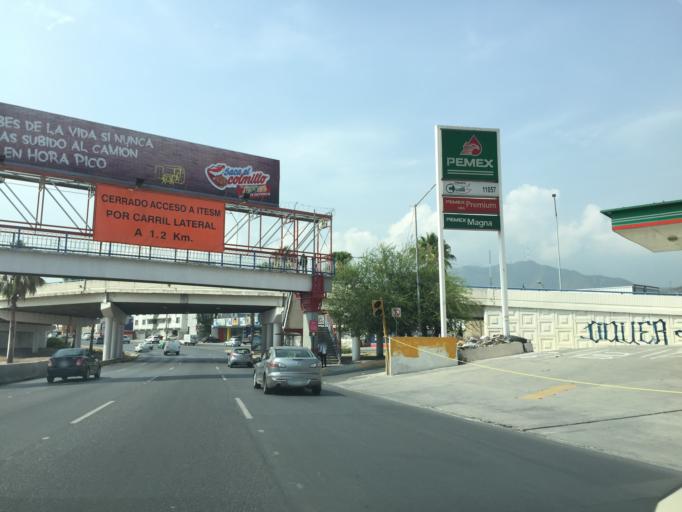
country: MX
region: Nuevo Leon
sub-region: Monterrey
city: Monterrey
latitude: 25.6603
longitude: -100.2973
